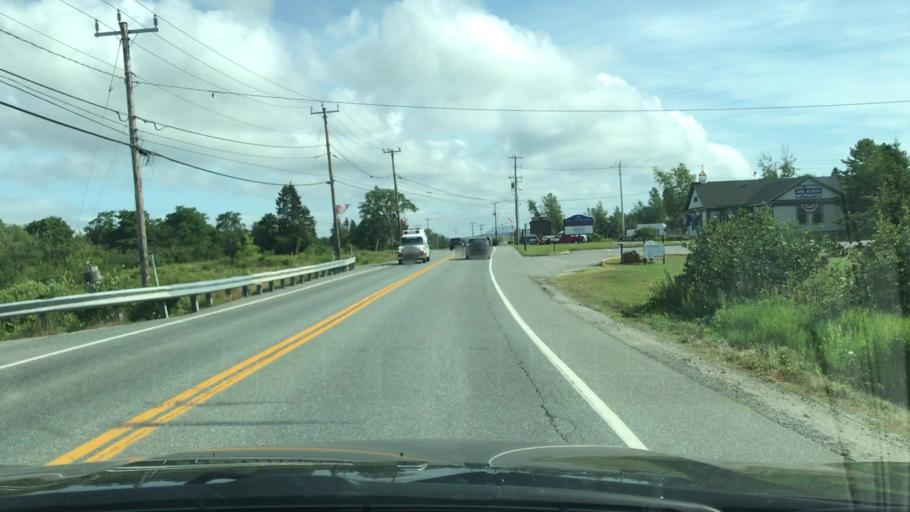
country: US
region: Maine
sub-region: Hancock County
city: Trenton
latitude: 44.4357
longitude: -68.3690
